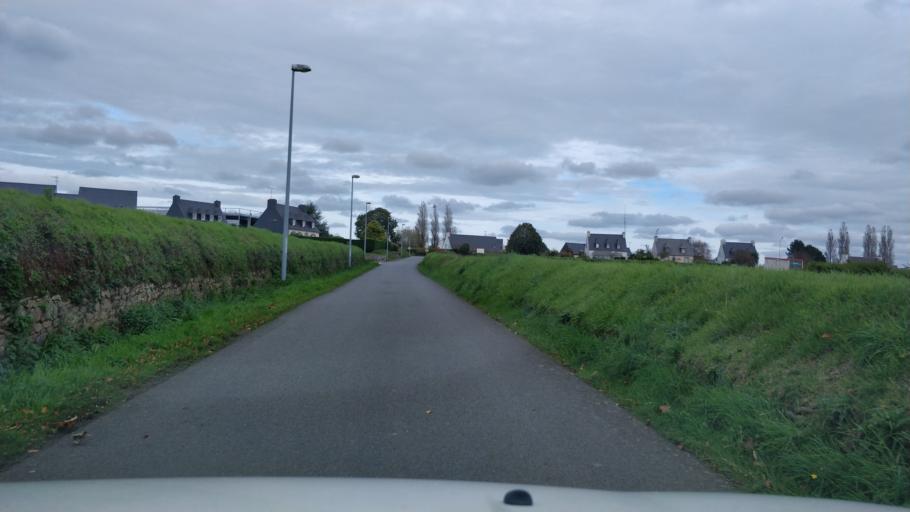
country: FR
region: Brittany
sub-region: Departement des Cotes-d'Armor
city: Minihy-Treguier
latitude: 48.7754
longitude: -3.2309
